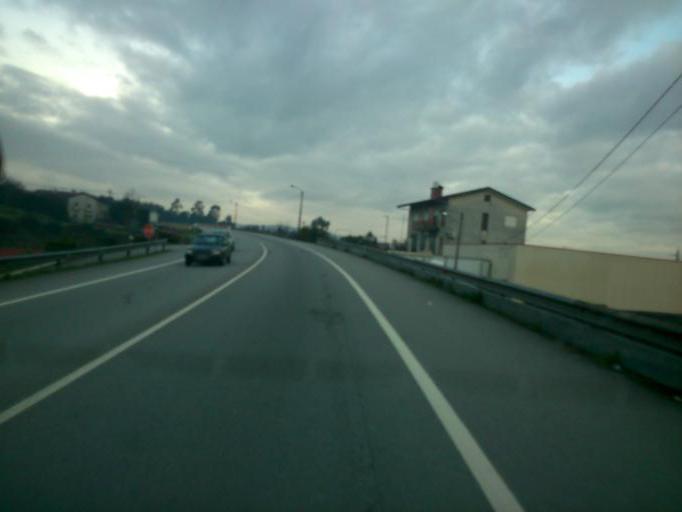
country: PT
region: Braga
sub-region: Barcelos
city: Barcelos
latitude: 41.5216
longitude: -8.5884
